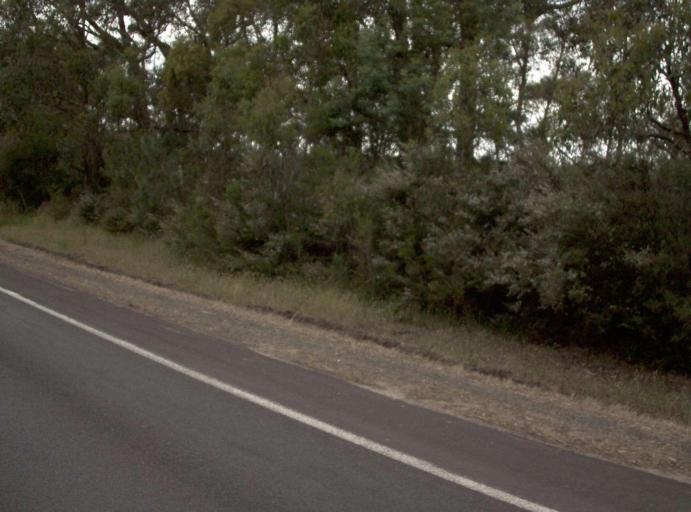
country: AU
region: Victoria
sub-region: Wellington
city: Sale
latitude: -38.4994
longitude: 146.8999
